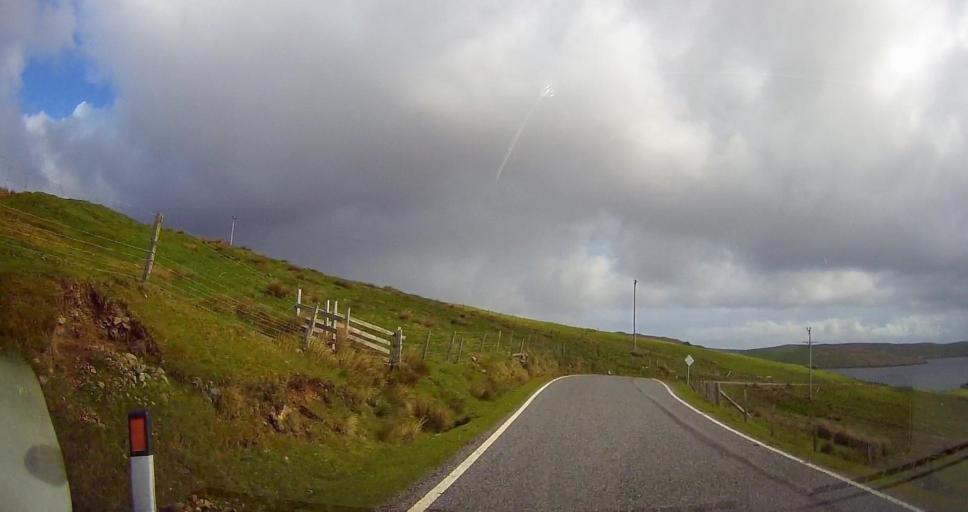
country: GB
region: Scotland
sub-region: Shetland Islands
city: Lerwick
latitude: 60.5289
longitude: -1.3671
